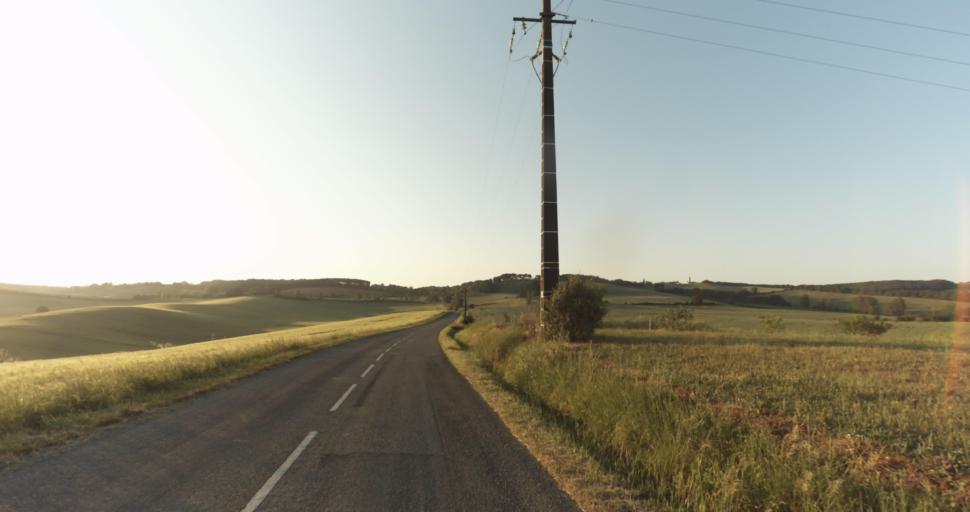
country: FR
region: Midi-Pyrenees
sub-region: Departement du Gers
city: Pujaudran
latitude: 43.6268
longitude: 1.1607
